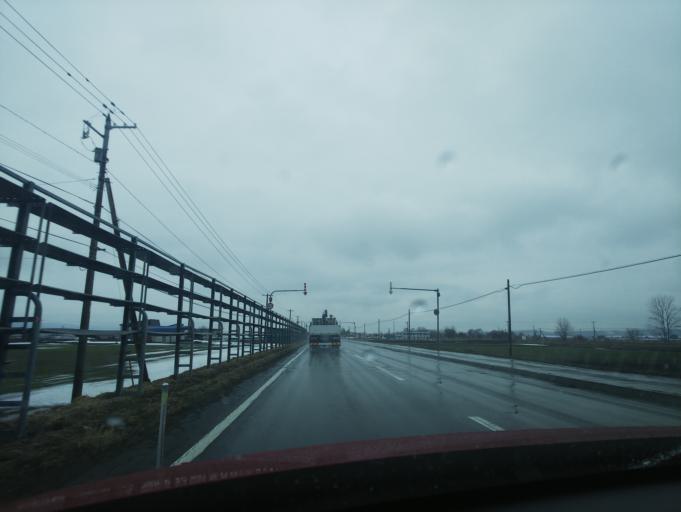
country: JP
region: Hokkaido
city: Nayoro
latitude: 44.2038
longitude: 142.3949
